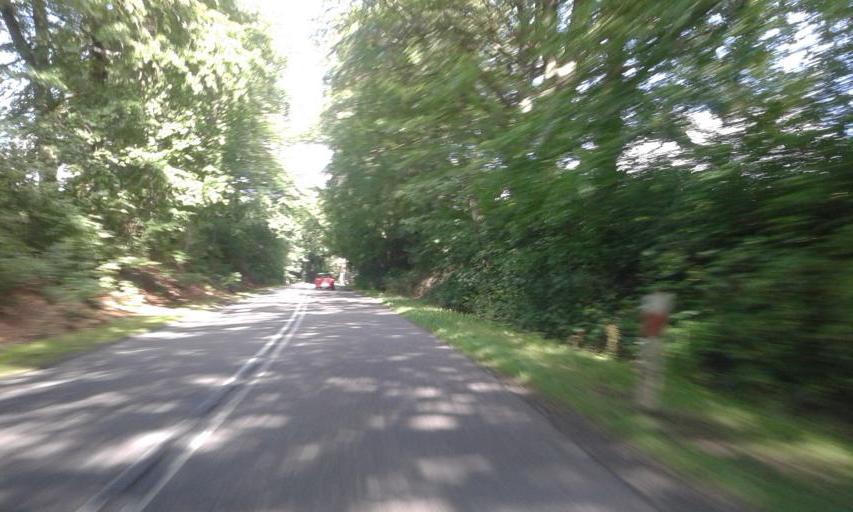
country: PL
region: West Pomeranian Voivodeship
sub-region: Powiat slawienski
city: Slawno
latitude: 54.2687
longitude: 16.6767
